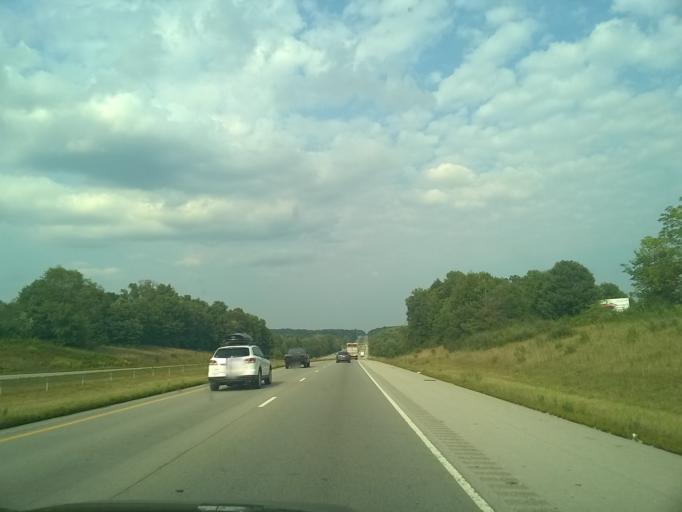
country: US
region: Indiana
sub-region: Clay County
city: Brazil
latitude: 39.4846
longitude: -87.0030
